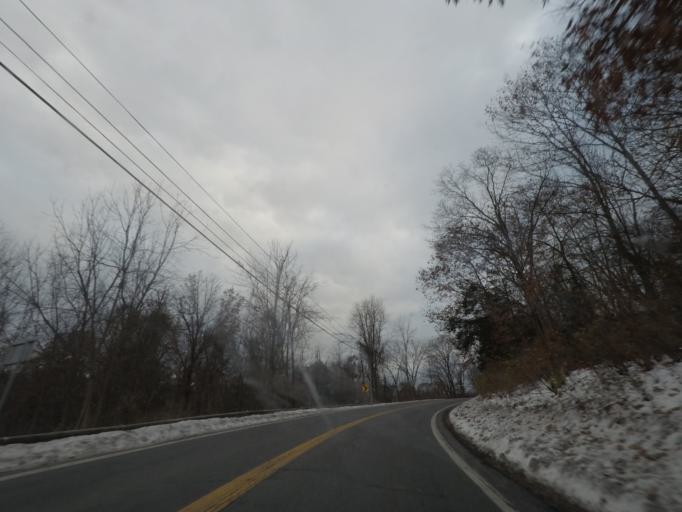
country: US
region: New York
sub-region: Ulster County
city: Clintondale
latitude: 41.6959
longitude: -74.1011
